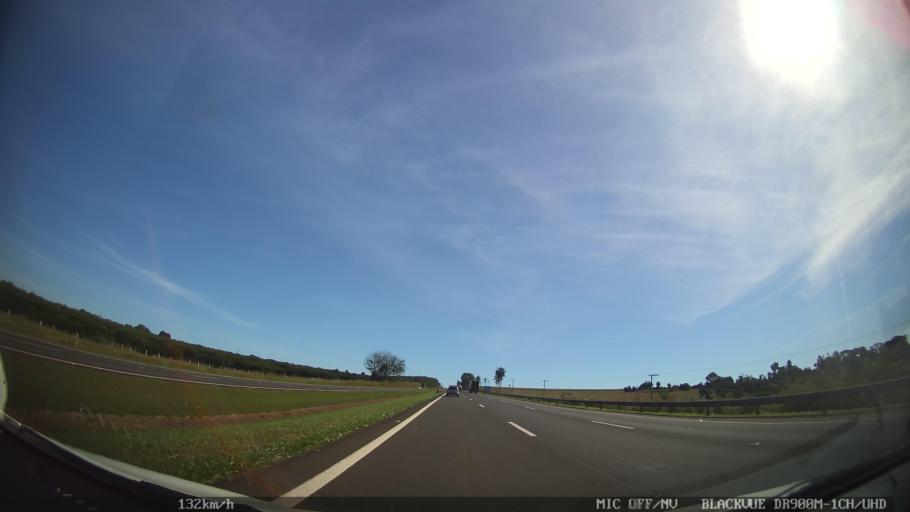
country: BR
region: Sao Paulo
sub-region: Porto Ferreira
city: Porto Ferreira
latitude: -21.7883
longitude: -47.5225
